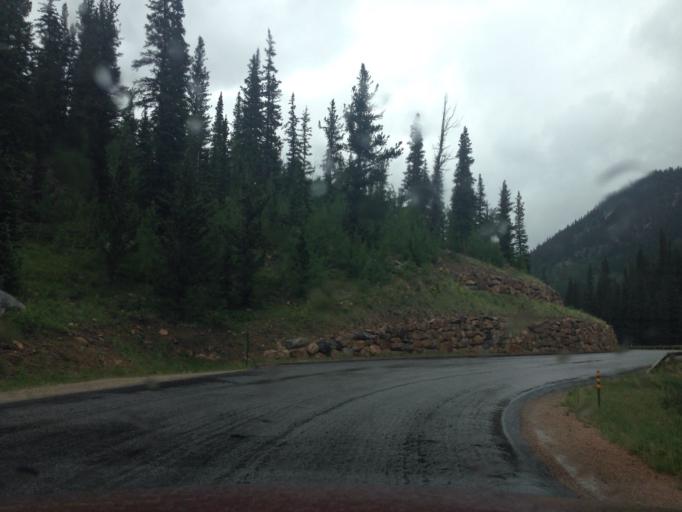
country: US
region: Colorado
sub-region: Clear Creek County
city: Georgetown
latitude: 39.6395
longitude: -105.7079
